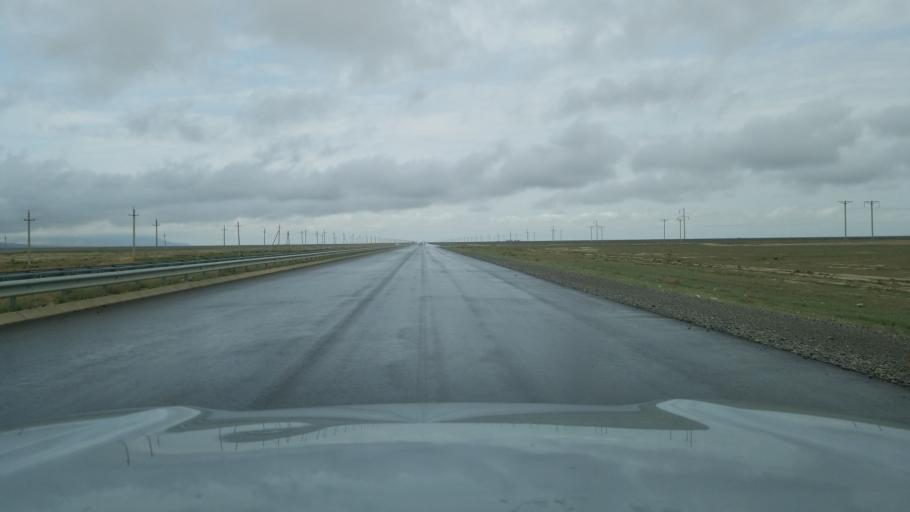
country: TM
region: Balkan
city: Gazanjyk
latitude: 39.1319
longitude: 55.8881
